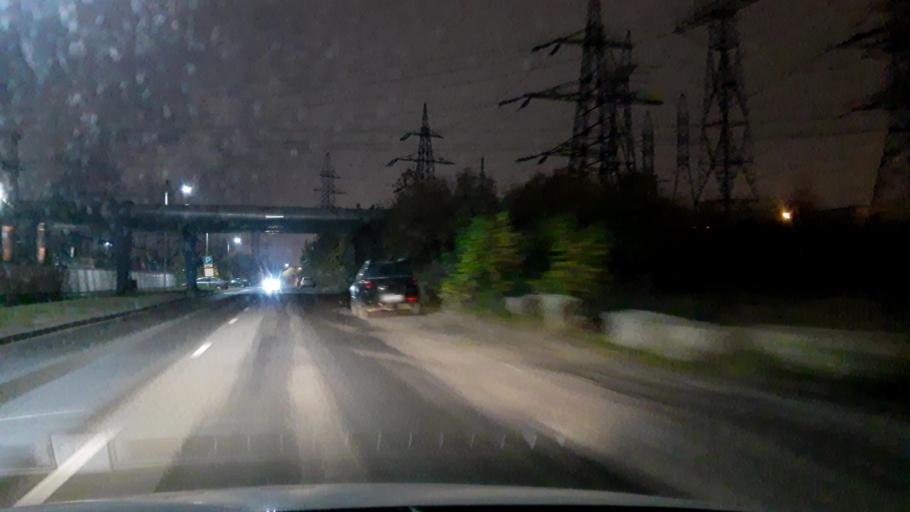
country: RU
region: Moskovskaya
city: Alekseyevka
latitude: 55.6362
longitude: 37.8157
